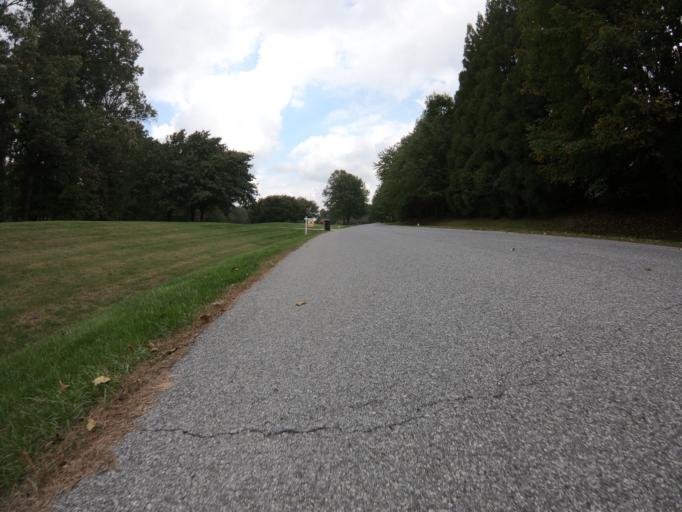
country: US
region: Maryland
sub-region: Howard County
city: Columbia
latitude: 39.2630
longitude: -76.8789
